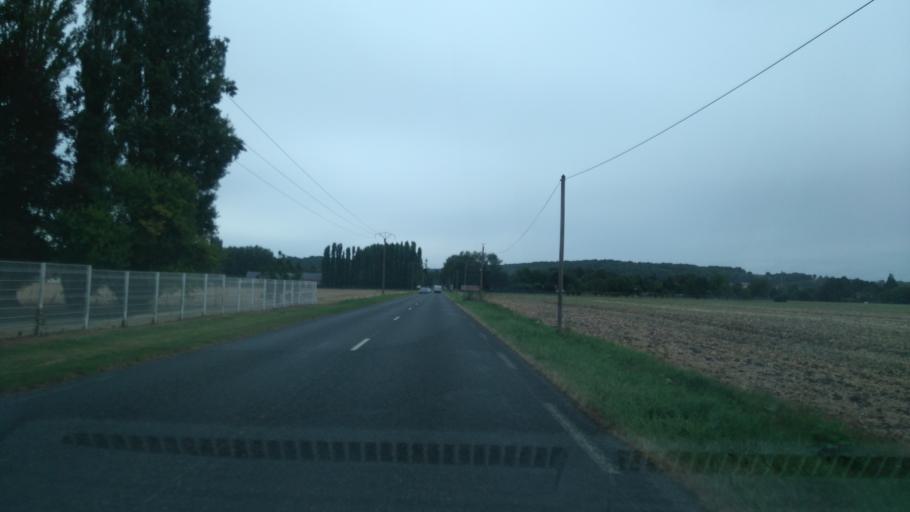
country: FR
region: Picardie
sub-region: Departement de l'Oise
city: Precy-sur-Oise
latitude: 49.1978
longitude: 2.3793
